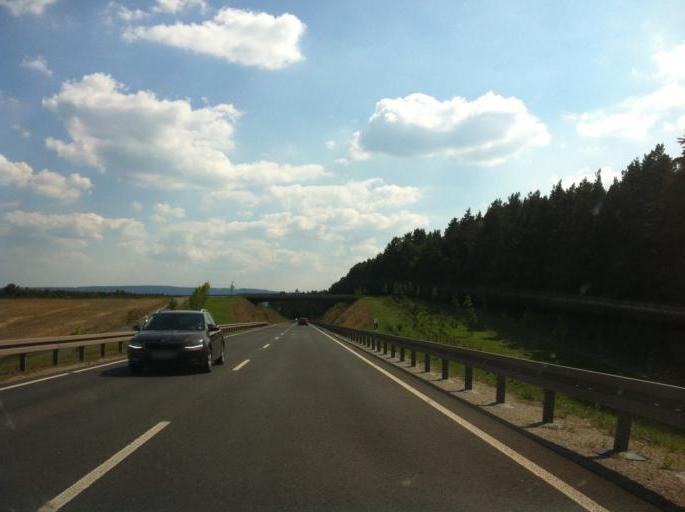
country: DE
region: Thuringia
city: Langewiesen
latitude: 50.6895
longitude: 10.9721
